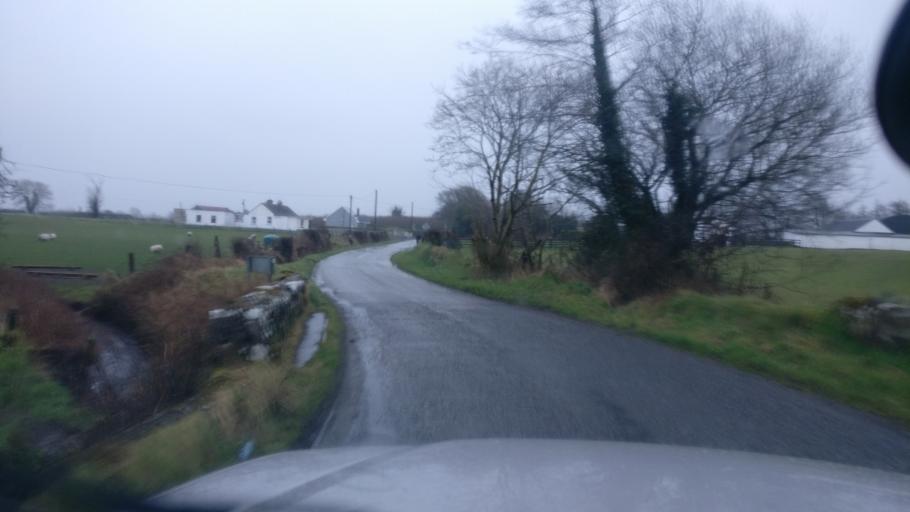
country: IE
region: Connaught
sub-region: County Galway
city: Ballinasloe
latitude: 53.3162
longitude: -8.3719
